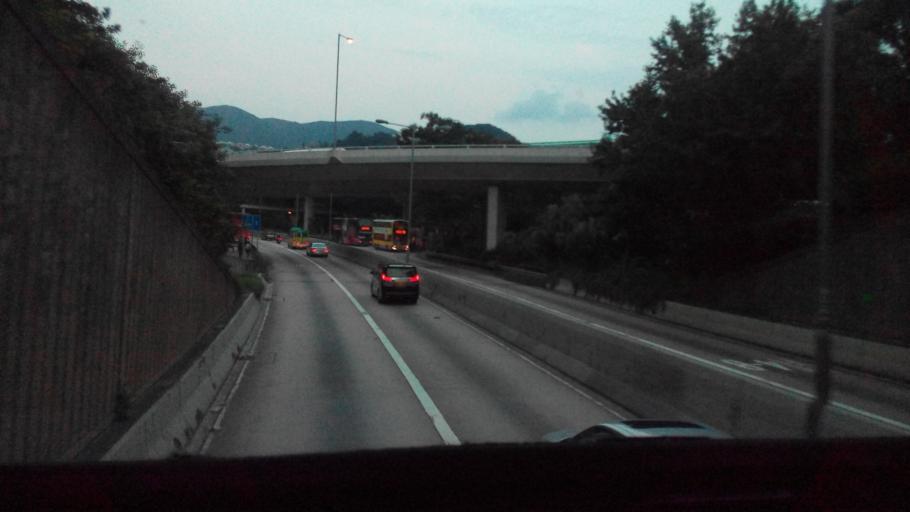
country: HK
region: Wanchai
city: Wan Chai
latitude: 22.2500
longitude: 114.1745
